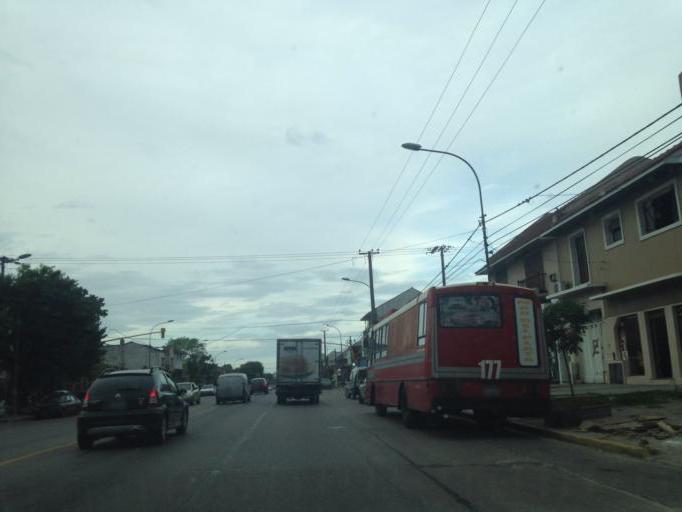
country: AR
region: Buenos Aires
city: Mar del Plata
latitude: -38.0249
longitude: -57.5782
